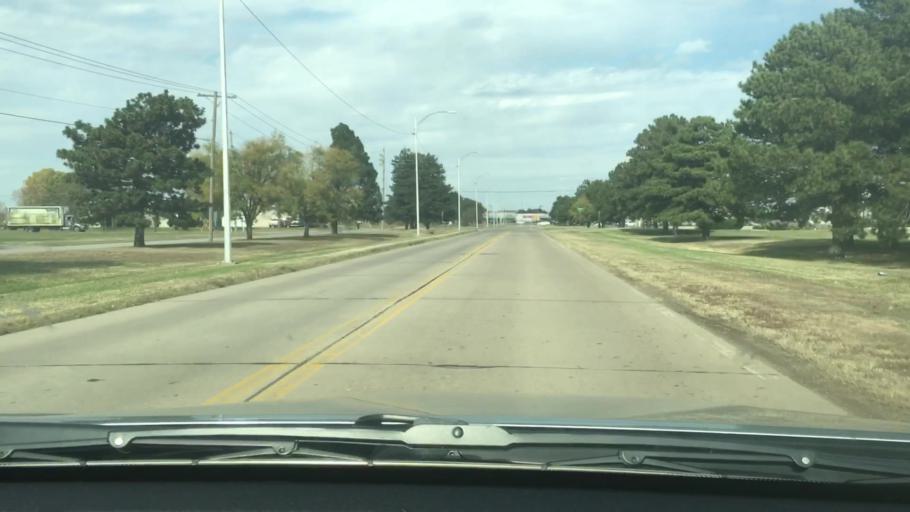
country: US
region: Kansas
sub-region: Sedgwick County
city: Wichita
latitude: 37.6679
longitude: -97.4212
